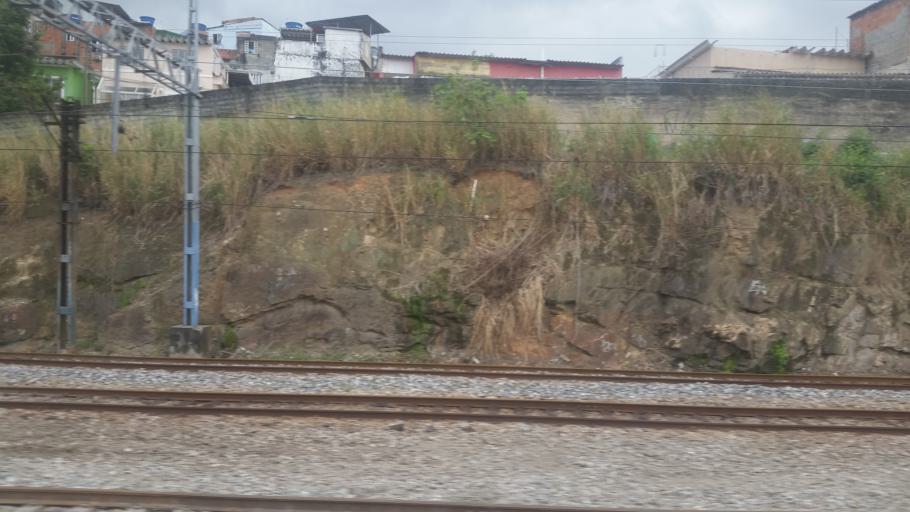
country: BR
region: Rio de Janeiro
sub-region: Sao Joao De Meriti
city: Sao Joao de Meriti
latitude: -22.8840
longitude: -43.3267
